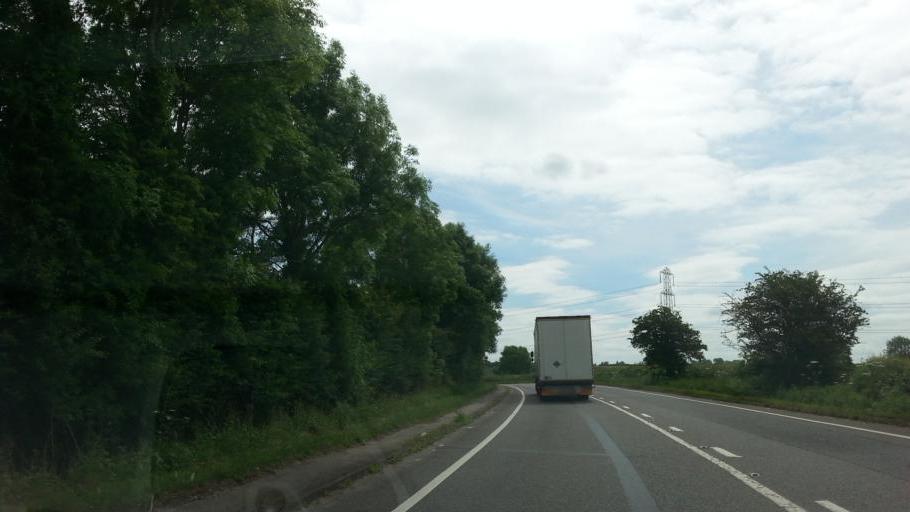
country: GB
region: England
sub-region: Nottinghamshire
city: Cotgrave
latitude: 52.8888
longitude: -1.0799
